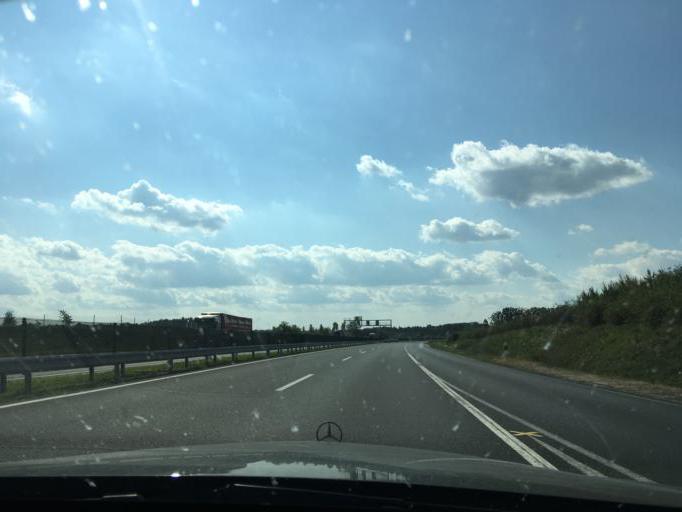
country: HU
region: Zala
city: Zalakomar
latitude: 46.5102
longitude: 17.1887
